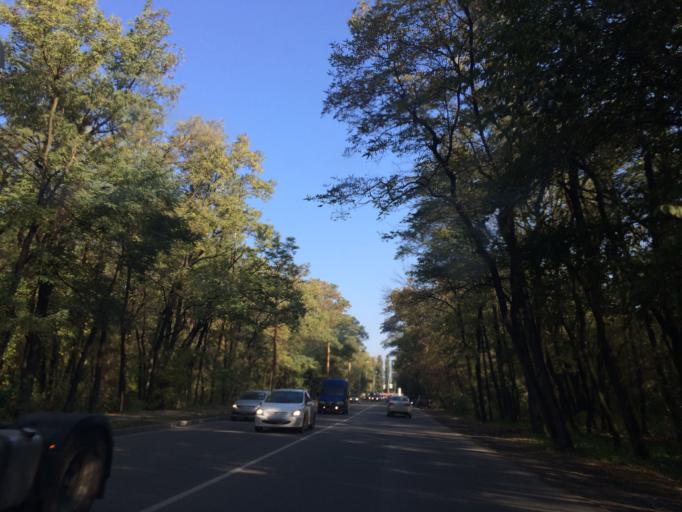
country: RU
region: Rostov
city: Imeni Chkalova
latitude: 47.2757
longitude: 39.7956
